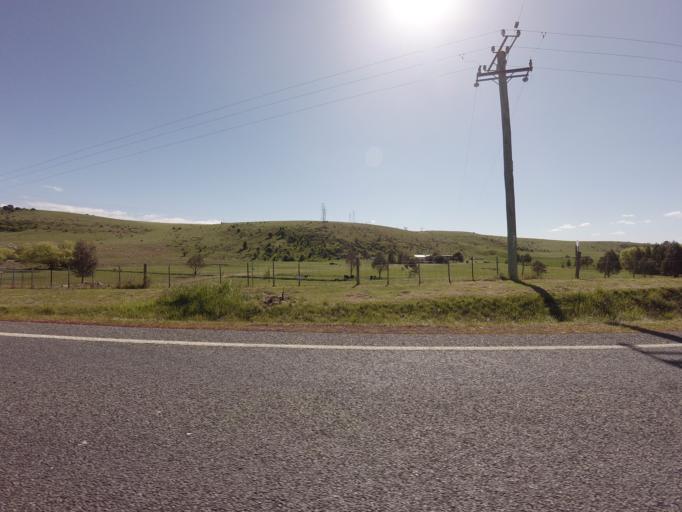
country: AU
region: Tasmania
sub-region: Derwent Valley
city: New Norfolk
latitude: -42.6624
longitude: 146.9340
